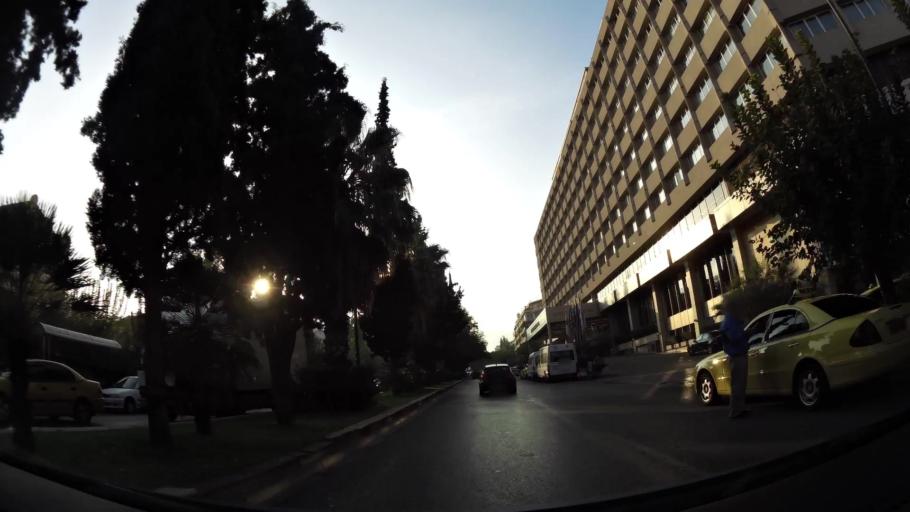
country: GR
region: Attica
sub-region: Nomarchia Athinas
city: Vyronas
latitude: 37.9736
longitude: 23.7513
